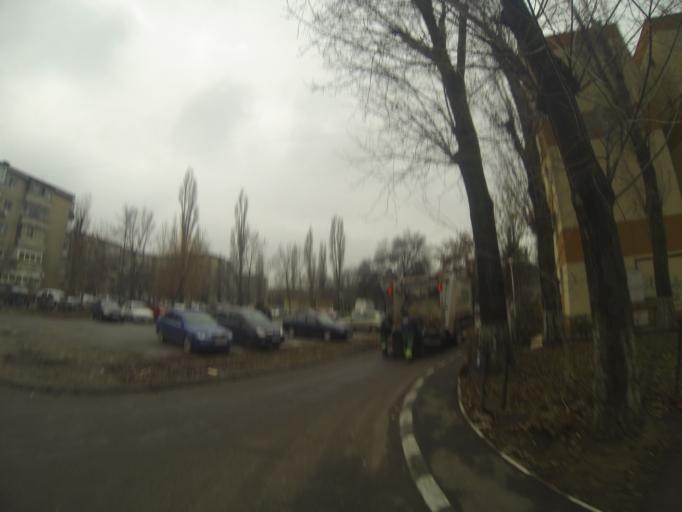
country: RO
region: Bucuresti
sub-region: Municipiul Bucuresti
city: Bucuresti
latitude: 44.4060
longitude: 26.0733
